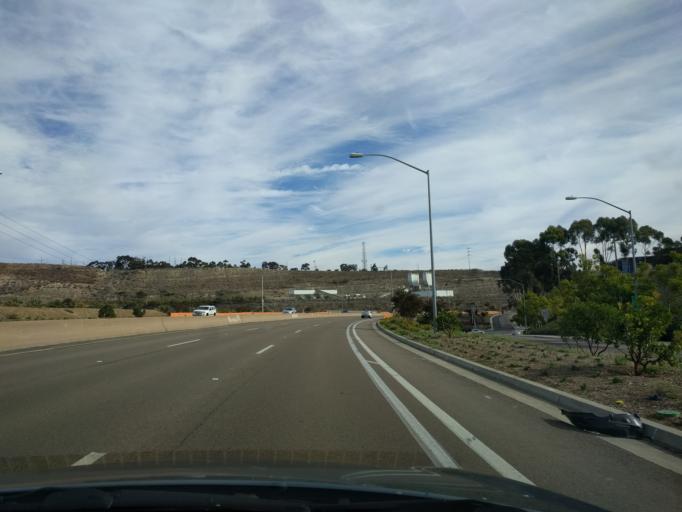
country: US
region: California
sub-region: San Diego County
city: San Diego
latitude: 32.7772
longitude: -117.1438
